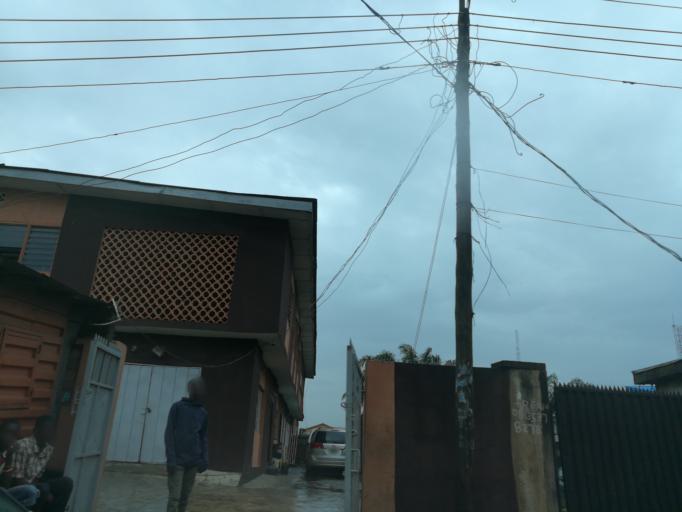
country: NG
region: Lagos
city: Oshodi
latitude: 6.5546
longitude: 3.3436
